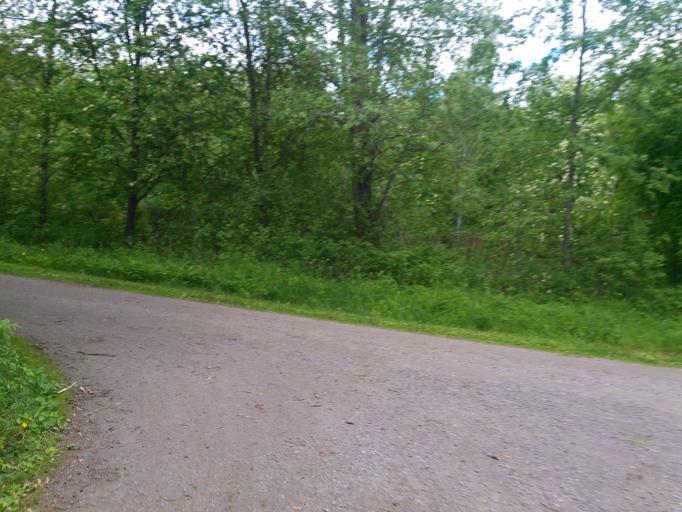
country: SE
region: Vaesterbotten
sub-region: Umea Kommun
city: Umea
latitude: 63.8246
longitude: 20.2390
